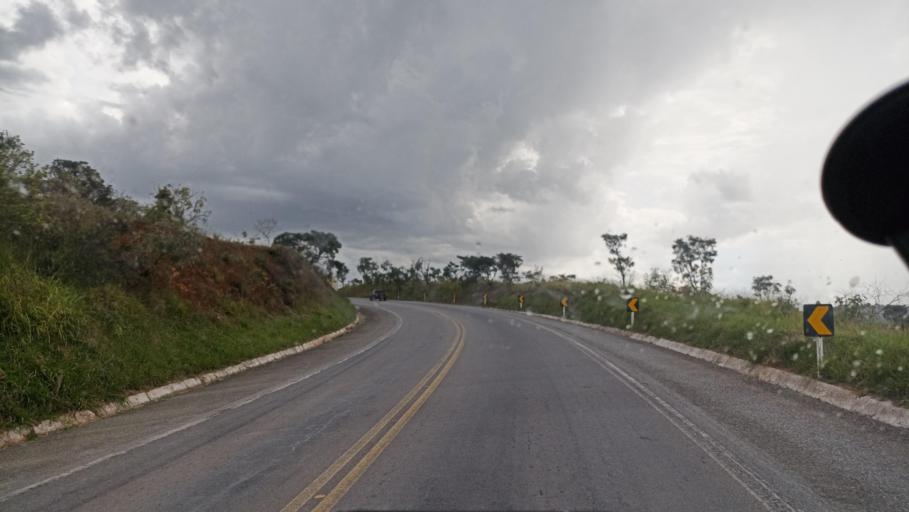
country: BR
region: Minas Gerais
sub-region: Baependi
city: Baependi
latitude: -21.9233
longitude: -44.8233
